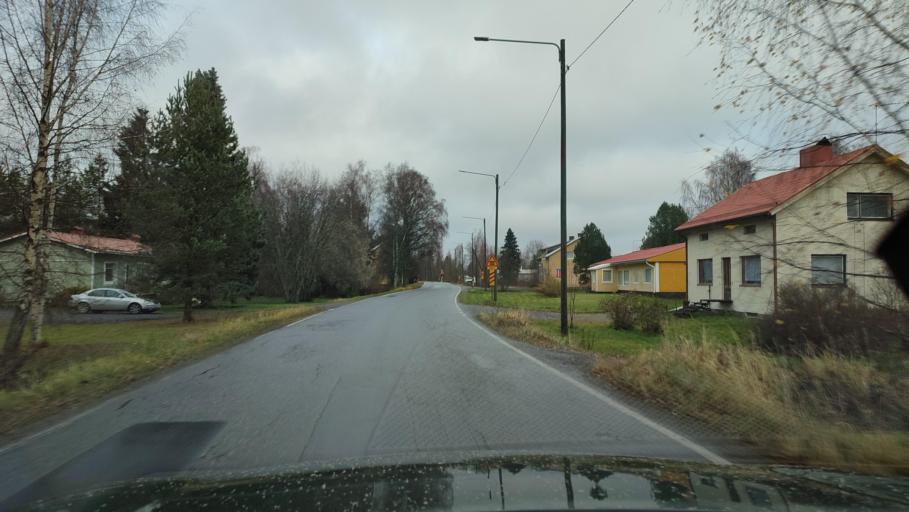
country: FI
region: Southern Ostrobothnia
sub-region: Suupohja
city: Teuva
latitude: 62.4535
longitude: 21.6035
